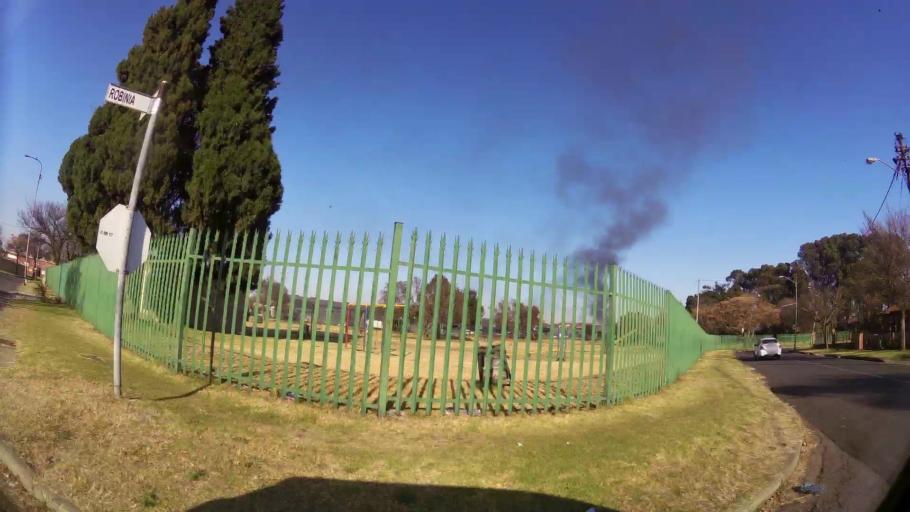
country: ZA
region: Gauteng
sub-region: Ekurhuleni Metropolitan Municipality
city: Germiston
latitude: -26.2025
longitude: 28.1285
